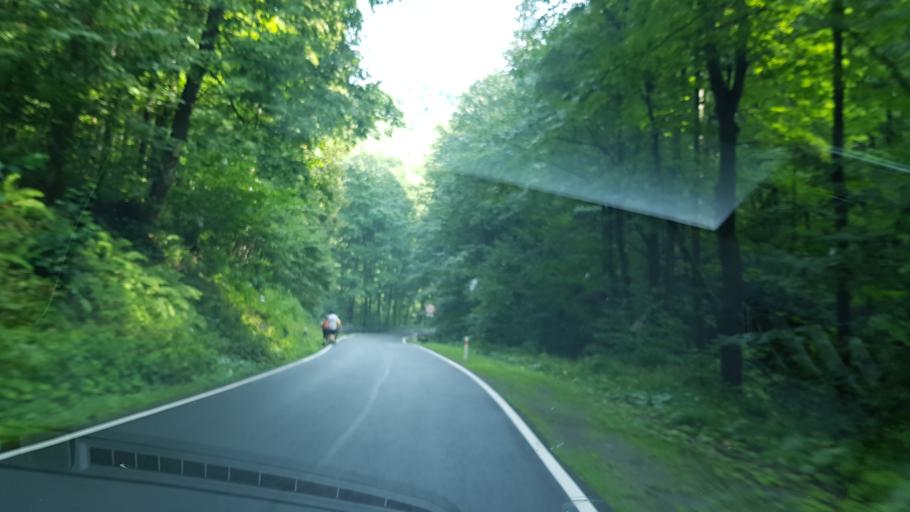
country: CZ
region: Olomoucky
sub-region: Okres Jesenik
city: Jesenik
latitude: 50.2072
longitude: 17.2447
